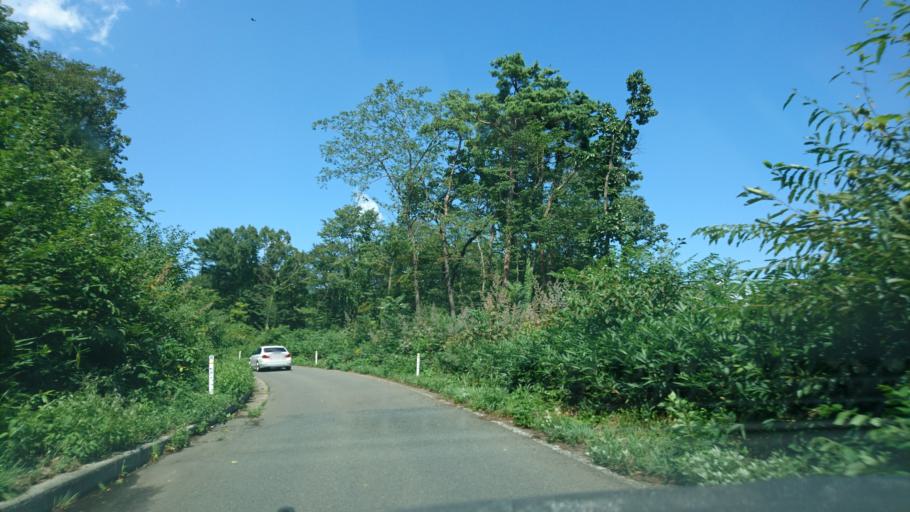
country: JP
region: Iwate
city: Morioka-shi
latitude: 39.8060
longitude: 141.1262
